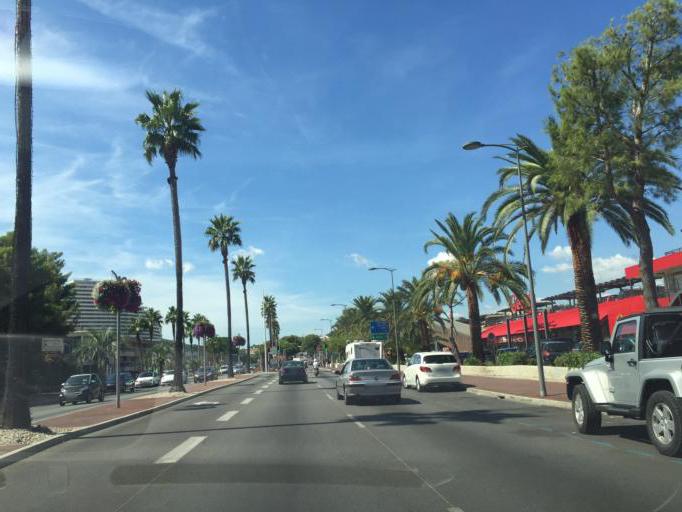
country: FR
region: Provence-Alpes-Cote d'Azur
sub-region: Departement des Alpes-Maritimes
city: Cagnes-sur-Mer
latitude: 43.6408
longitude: 7.1410
